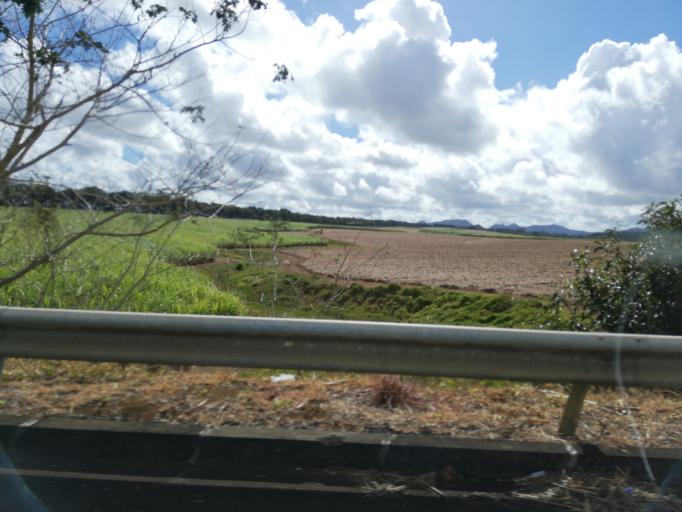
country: MU
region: Grand Port
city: Beau Vallon
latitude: -20.4056
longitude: 57.6755
